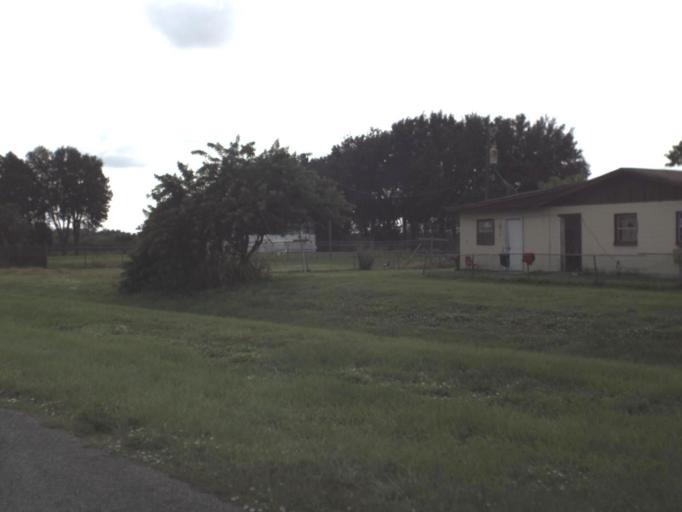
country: US
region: Florida
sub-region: Lee County
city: Alva
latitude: 26.7091
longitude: -81.5802
